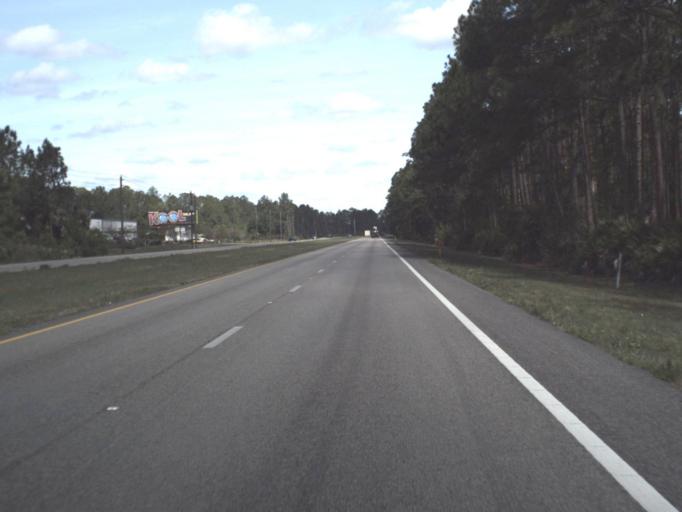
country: US
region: Florida
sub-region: Flagler County
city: Flagler Beach
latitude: 29.3796
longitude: -81.1837
